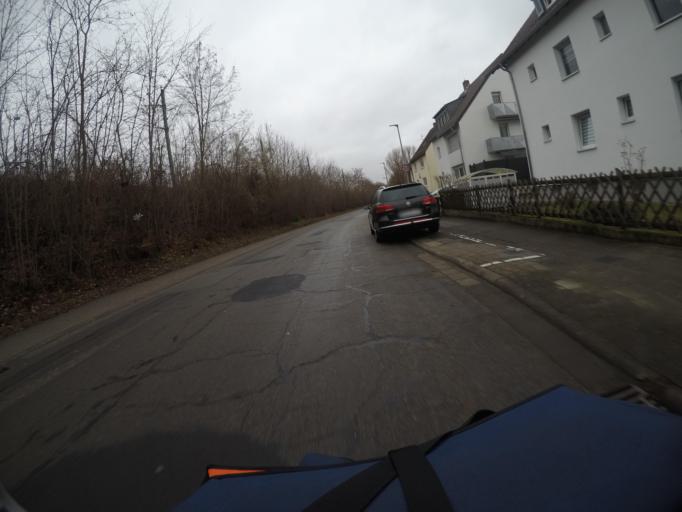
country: DE
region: Rheinland-Pfalz
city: Germersheim
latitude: 49.2205
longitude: 8.3796
